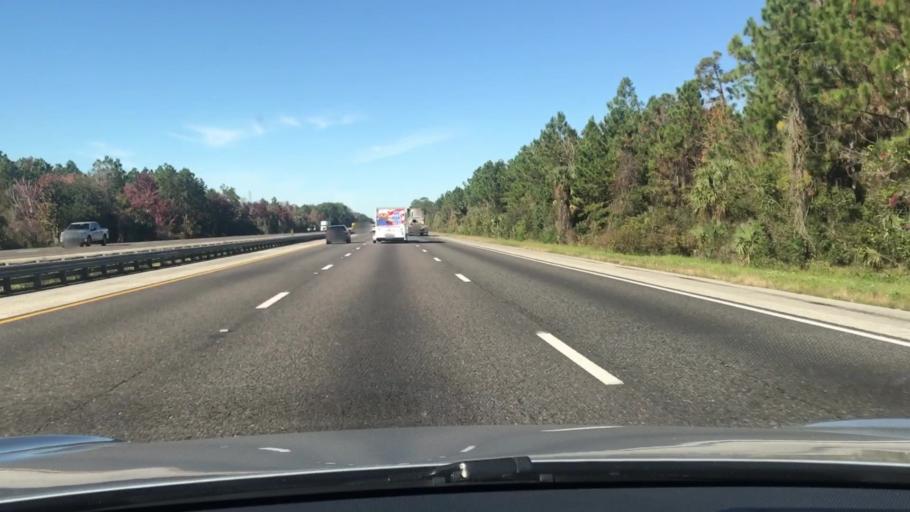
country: US
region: Florida
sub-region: Flagler County
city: Palm Coast
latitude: 29.6263
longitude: -81.2624
